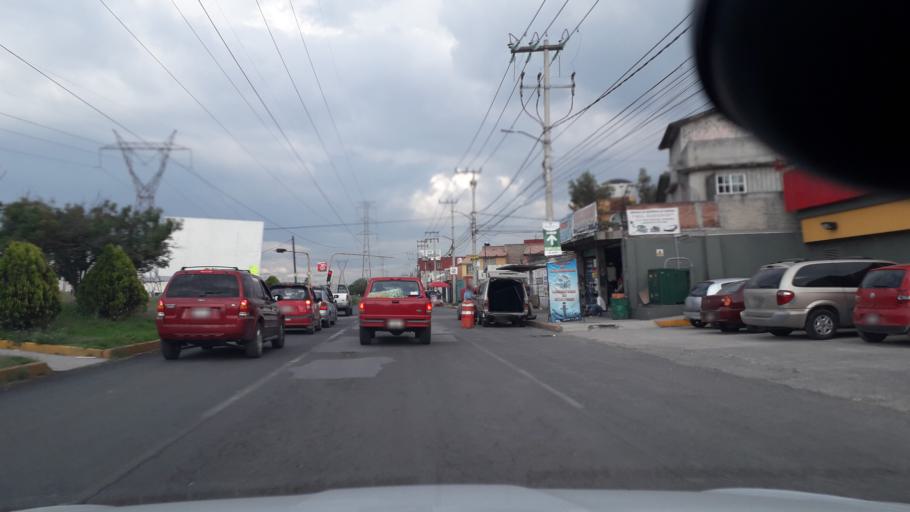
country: MX
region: Mexico
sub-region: Tultitlan
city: Fuentes del Valle
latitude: 19.6408
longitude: -99.1288
